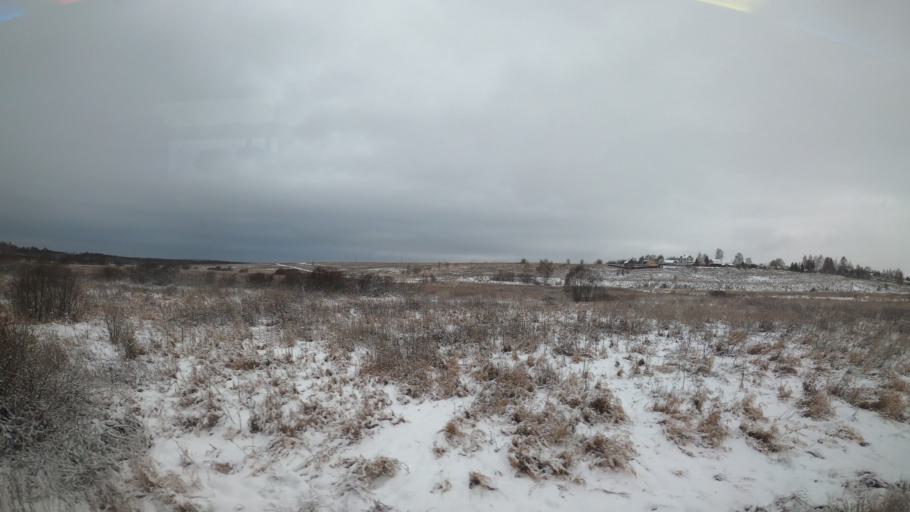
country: RU
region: Jaroslavl
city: Pereslavl'-Zalesskiy
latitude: 56.6990
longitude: 38.9150
